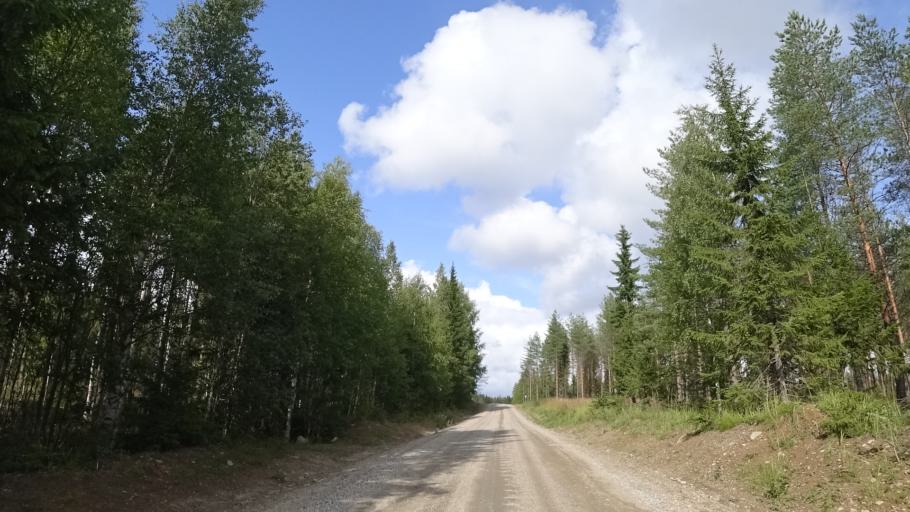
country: FI
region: North Karelia
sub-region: Pielisen Karjala
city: Lieksa
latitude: 63.5926
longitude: 30.1370
